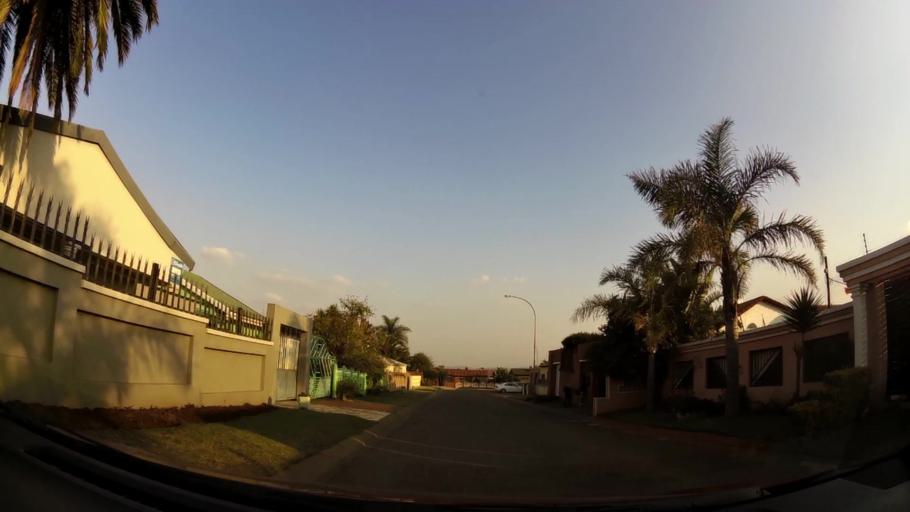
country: ZA
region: Gauteng
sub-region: City of Johannesburg Metropolitan Municipality
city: Soweto
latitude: -26.2847
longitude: 27.9030
